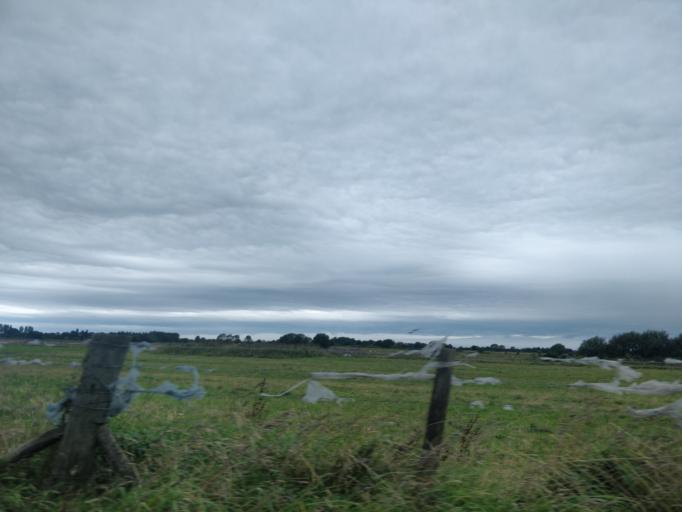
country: GB
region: England
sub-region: Lancashire
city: Ormskirk
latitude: 53.5944
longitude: -2.8631
